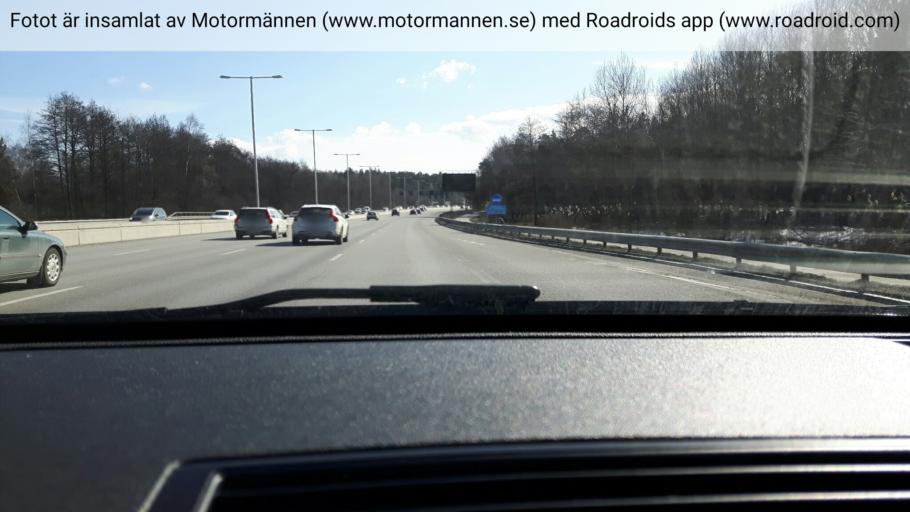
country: SE
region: Stockholm
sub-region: Solna Kommun
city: Rasunda
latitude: 59.3917
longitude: 17.9747
